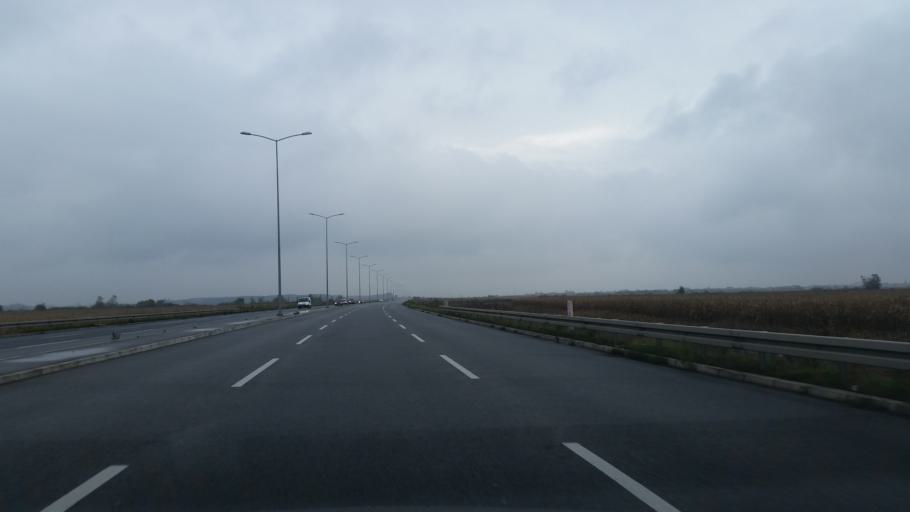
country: RS
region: Central Serbia
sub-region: Belgrade
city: Zemun
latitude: 44.8977
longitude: 20.4218
